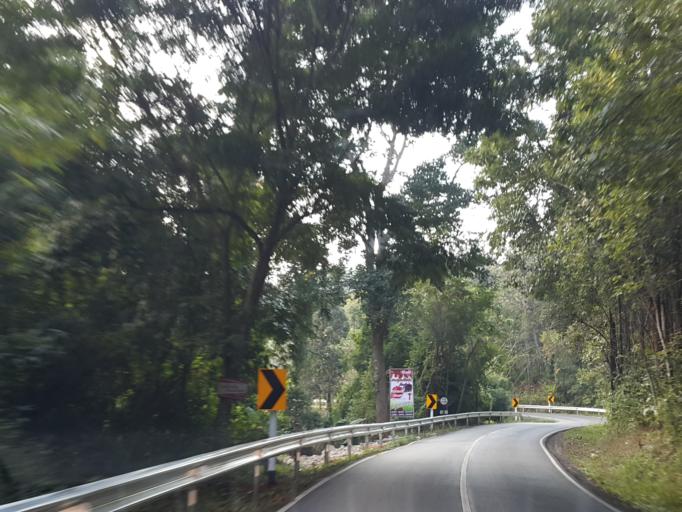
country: TH
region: Chiang Mai
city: Mae On
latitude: 18.8469
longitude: 99.2802
